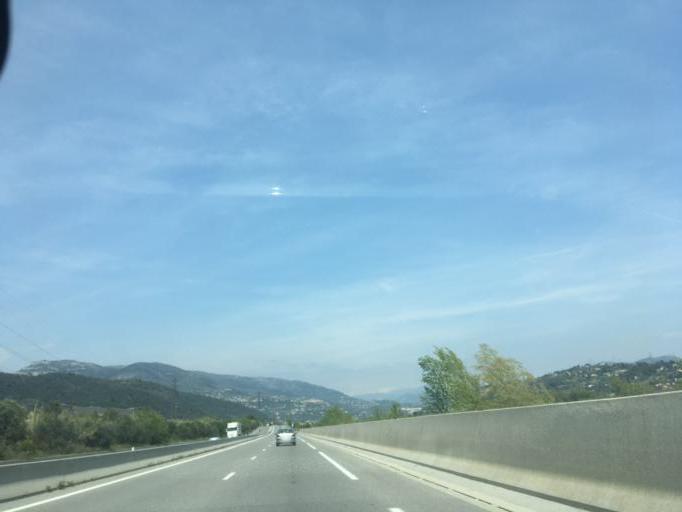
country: FR
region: Provence-Alpes-Cote d'Azur
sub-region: Departement des Alpes-Maritimes
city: La Gaude
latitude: 43.7076
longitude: 7.1843
